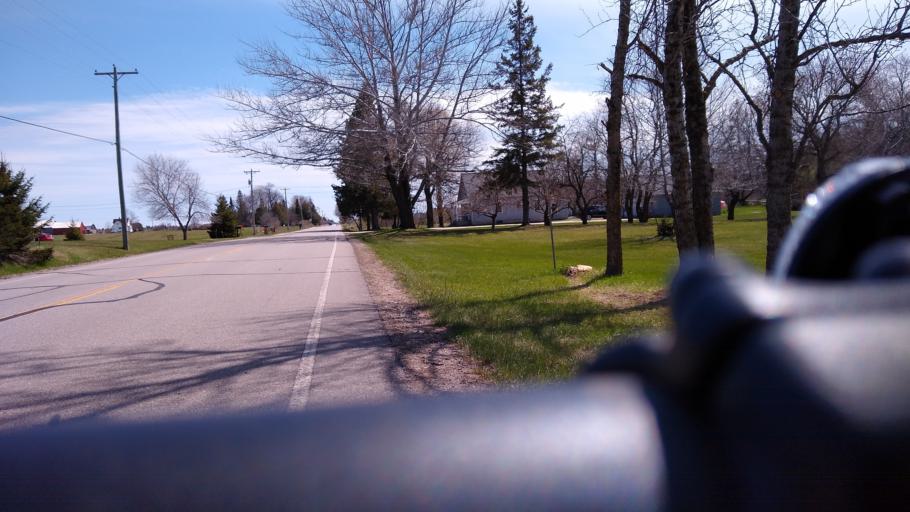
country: US
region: Michigan
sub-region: Delta County
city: Escanaba
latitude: 45.7216
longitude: -87.2025
